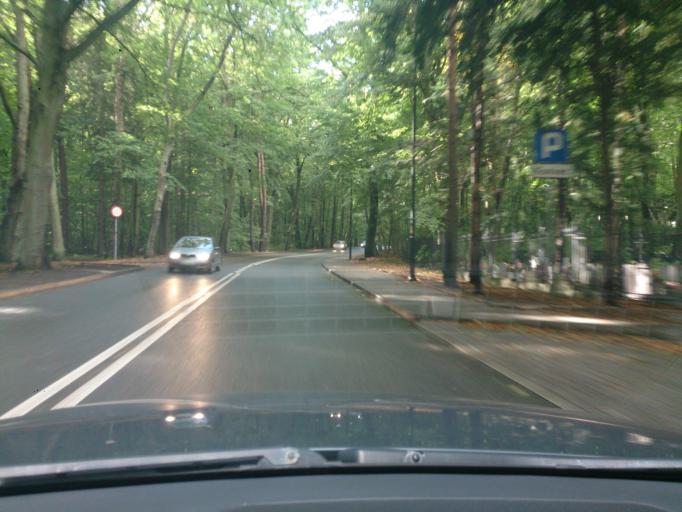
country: PL
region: Pomeranian Voivodeship
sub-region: Sopot
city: Sopot
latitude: 54.4514
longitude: 18.5445
